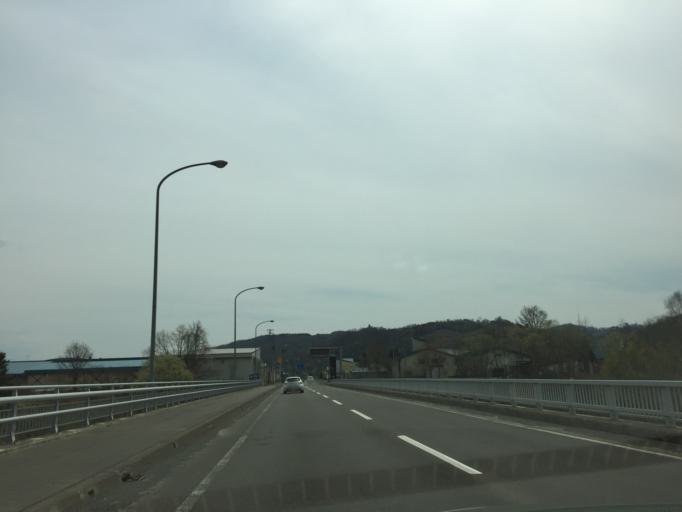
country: JP
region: Hokkaido
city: Ashibetsu
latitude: 43.5336
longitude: 142.1702
